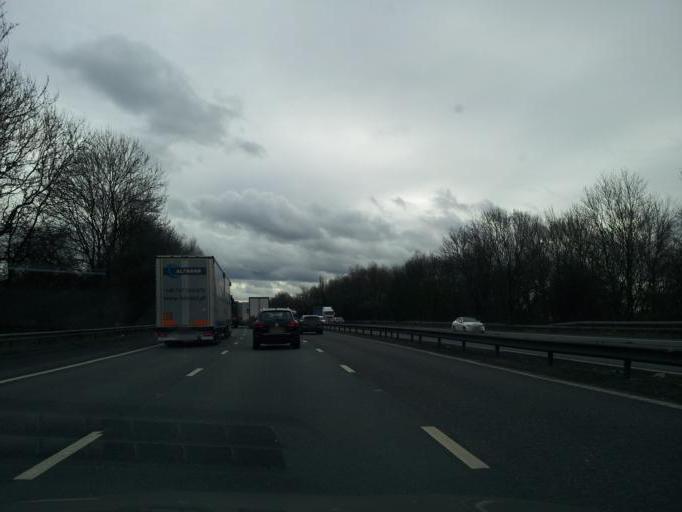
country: GB
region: England
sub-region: Staffordshire
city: Audley
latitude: 53.0086
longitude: -2.3293
